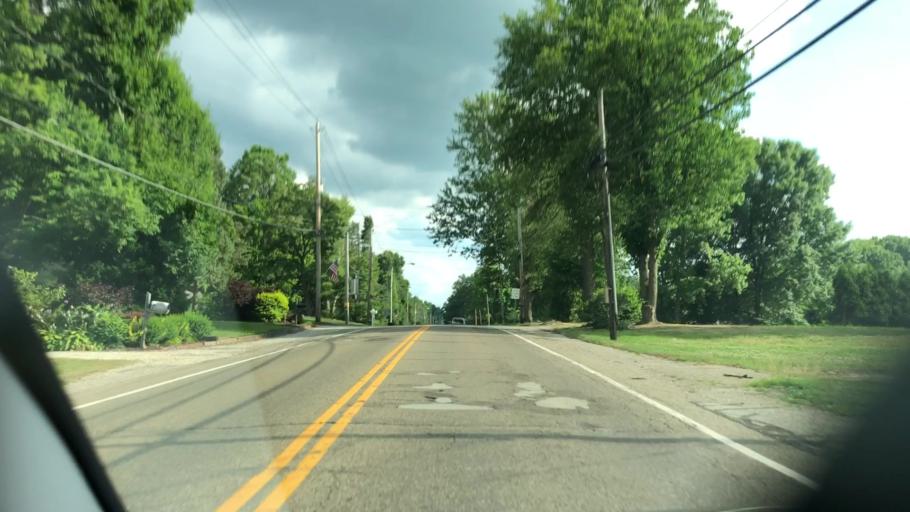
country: US
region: Ohio
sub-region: Summit County
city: Fairlawn
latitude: 41.0965
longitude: -81.6446
